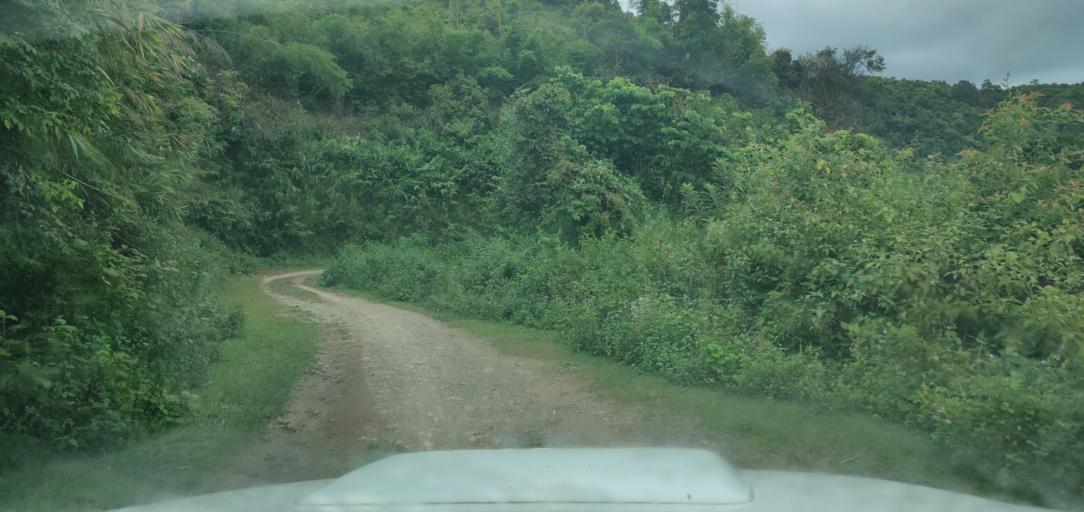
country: LA
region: Phongsali
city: Phongsali
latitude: 21.4468
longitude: 102.3102
